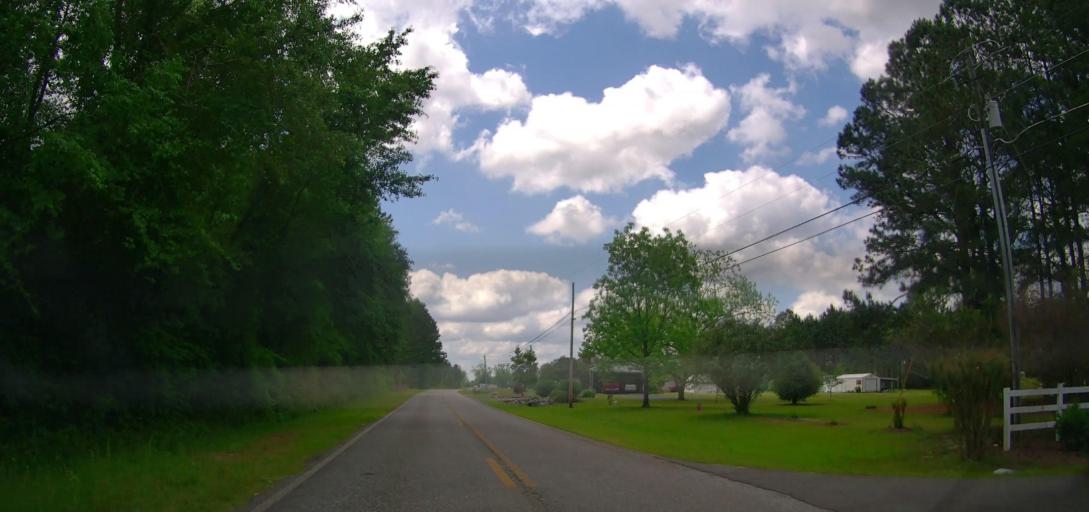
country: US
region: Georgia
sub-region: Laurens County
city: Dublin
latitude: 32.6043
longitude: -82.9484
